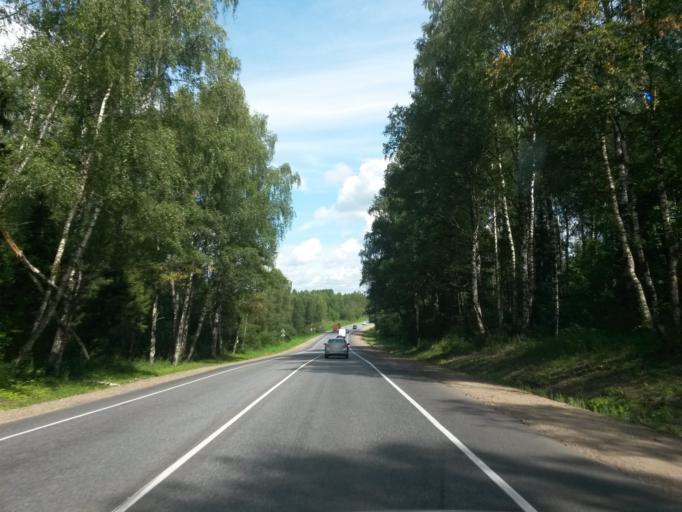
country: RU
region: Jaroslavl
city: Pereslavl'-Zalesskiy
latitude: 56.8193
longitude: 38.9047
